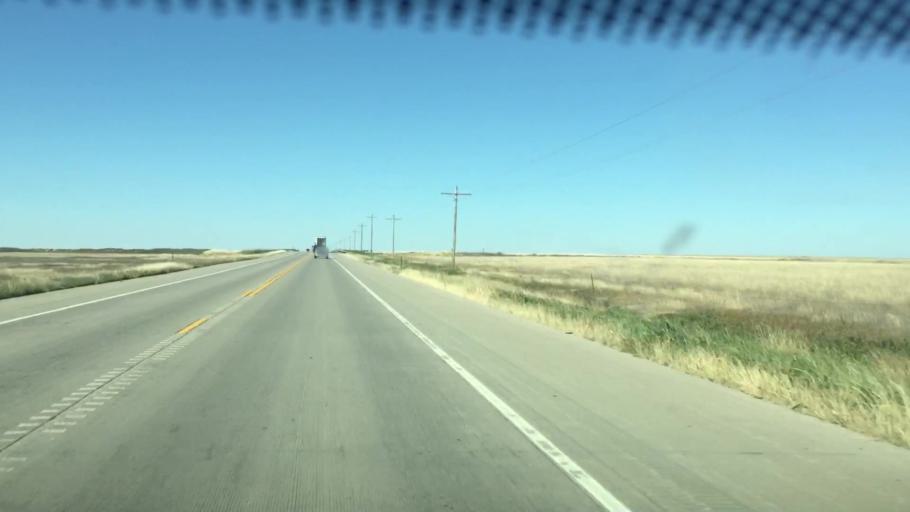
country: US
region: Colorado
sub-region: Prowers County
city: Lamar
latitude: 38.2352
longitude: -102.7240
